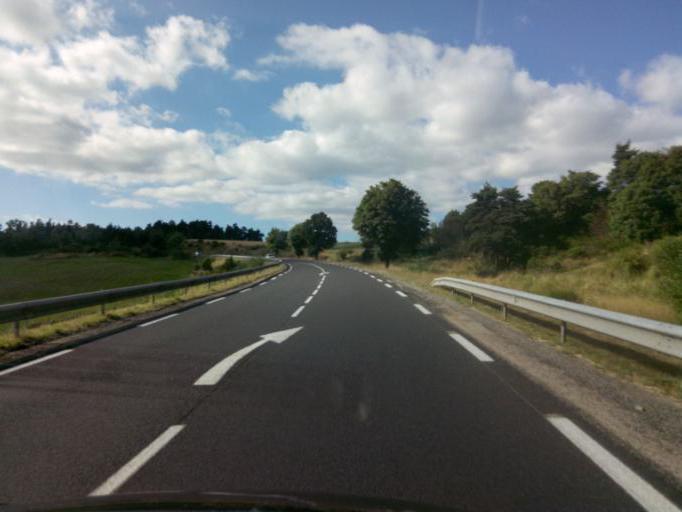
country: FR
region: Auvergne
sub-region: Departement de la Haute-Loire
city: Saint-Paulien
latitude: 45.1675
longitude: 3.8357
